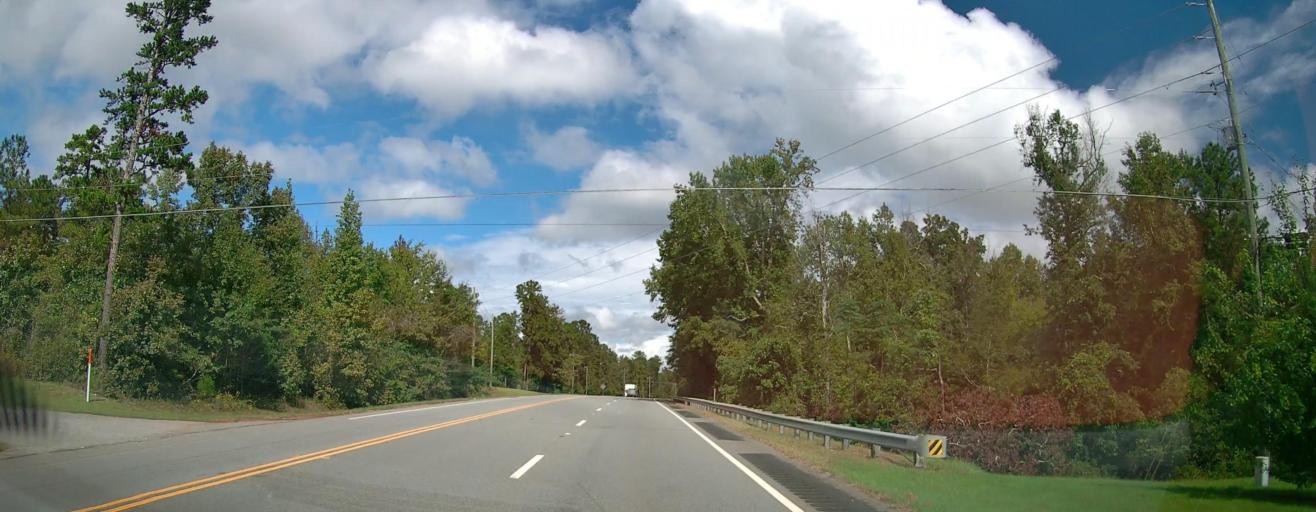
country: US
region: Georgia
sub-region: Baldwin County
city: Milledgeville
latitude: 33.0464
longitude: -83.2936
